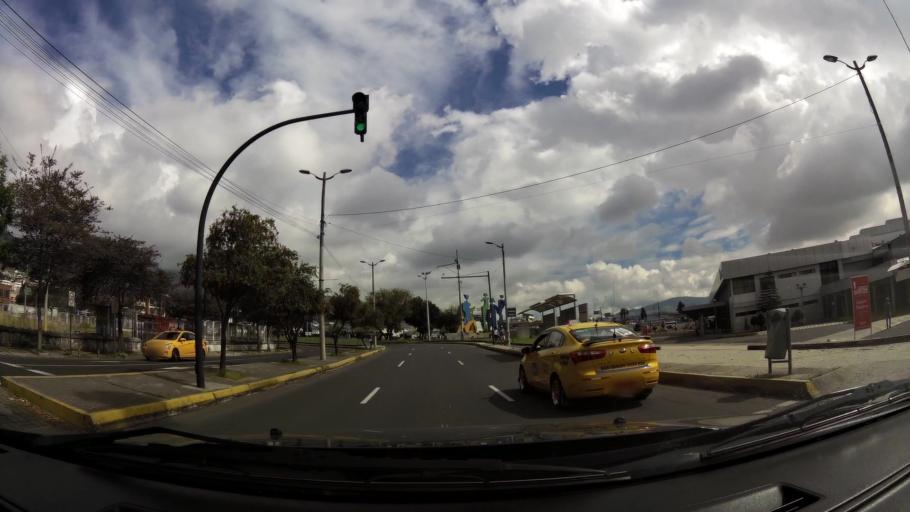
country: EC
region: Pichincha
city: Quito
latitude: -0.1463
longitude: -78.4904
